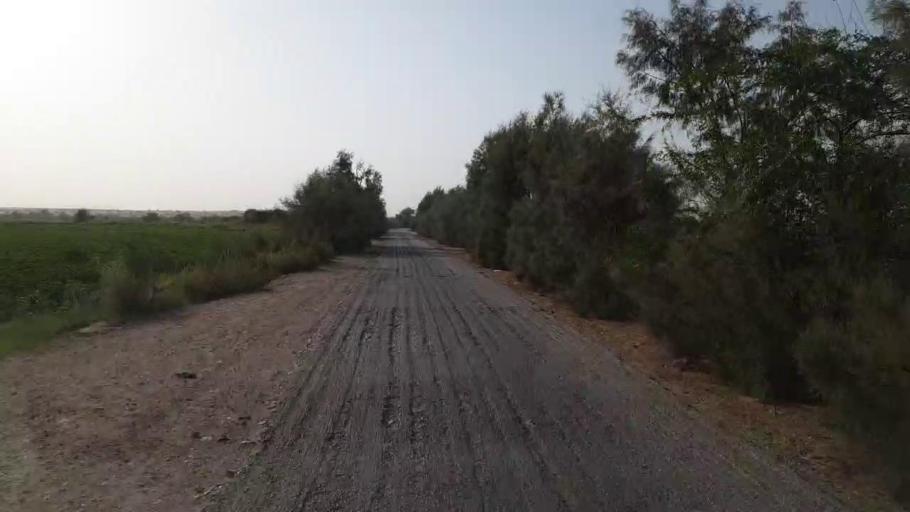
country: PK
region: Sindh
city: Jam Sahib
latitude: 26.4898
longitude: 68.8594
